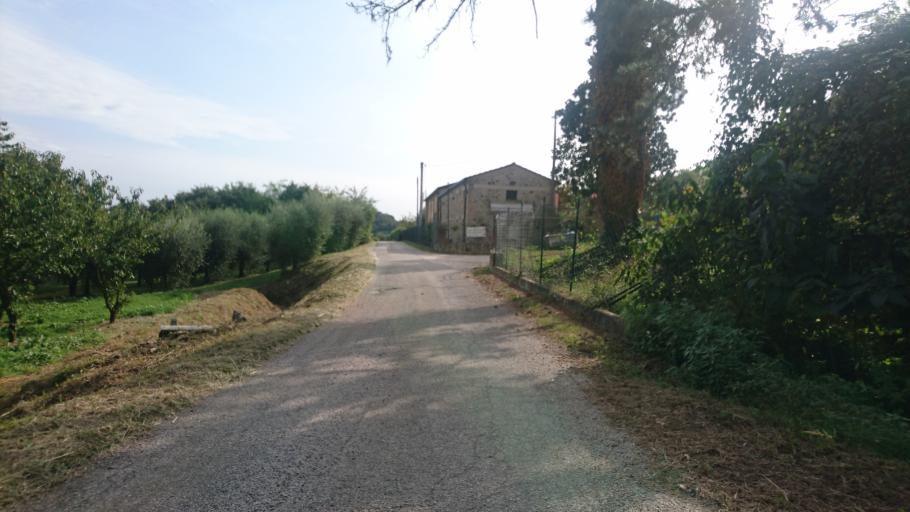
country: IT
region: Veneto
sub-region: Provincia di Padova
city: Arqua Petrarca
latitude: 45.2858
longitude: 11.7278
